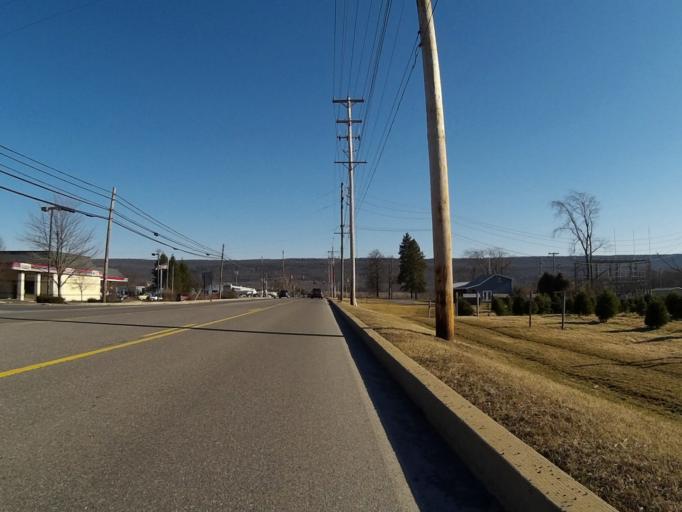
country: US
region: Pennsylvania
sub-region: Centre County
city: Pine Grove Mills
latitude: 40.7611
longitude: -77.8792
